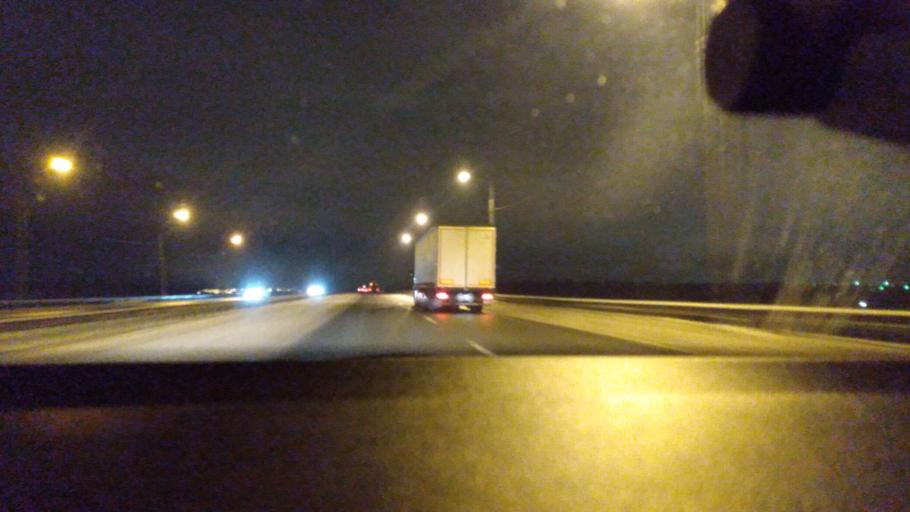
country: RU
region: Moskovskaya
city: Raduzhnyy
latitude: 55.1313
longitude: 38.7783
